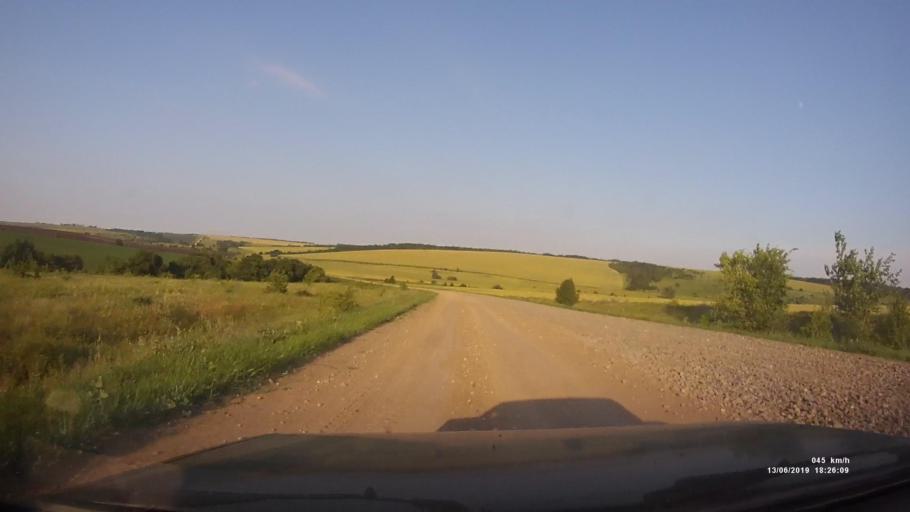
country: RU
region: Rostov
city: Kazanskaya
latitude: 49.8503
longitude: 41.3091
